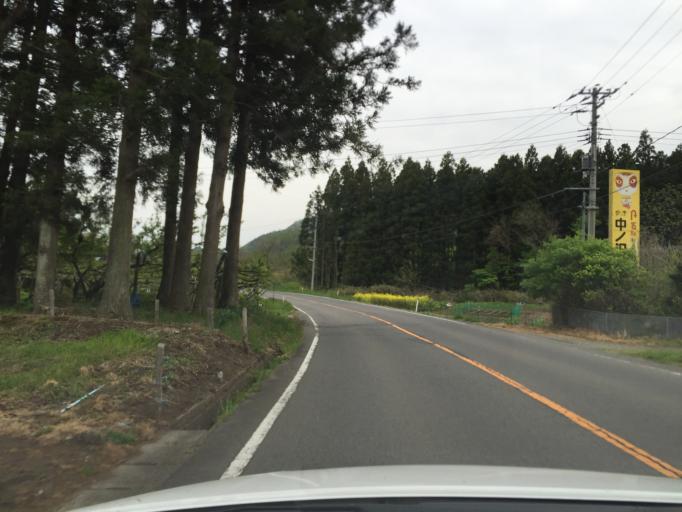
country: JP
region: Fukushima
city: Motomiya
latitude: 37.5142
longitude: 140.2699
